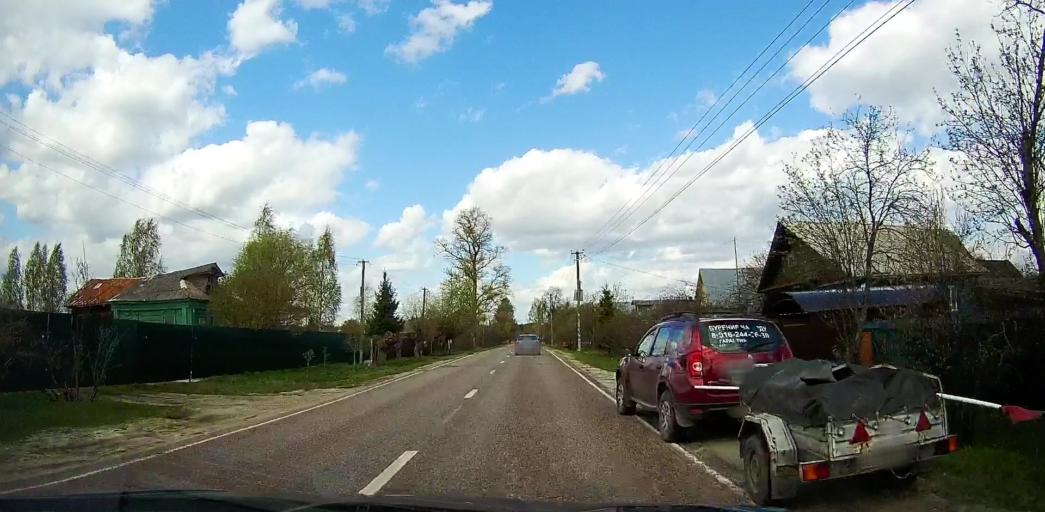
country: RU
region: Moskovskaya
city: Davydovo
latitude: 55.5838
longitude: 38.8270
